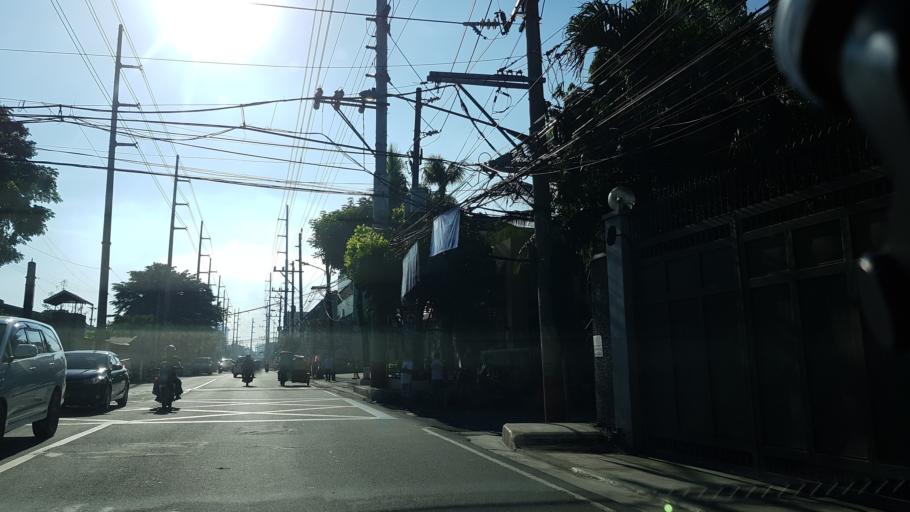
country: PH
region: Calabarzon
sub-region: Province of Rizal
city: Pateros
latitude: 14.5538
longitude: 121.0690
